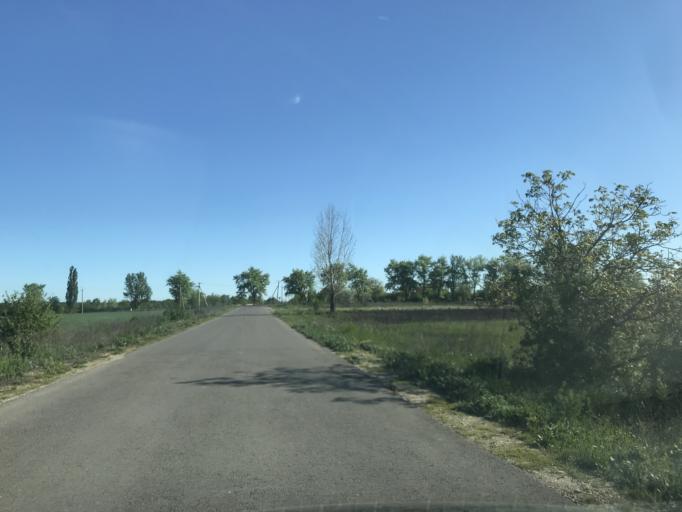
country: MD
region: Chisinau
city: Cricova
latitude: 47.2475
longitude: 28.8170
